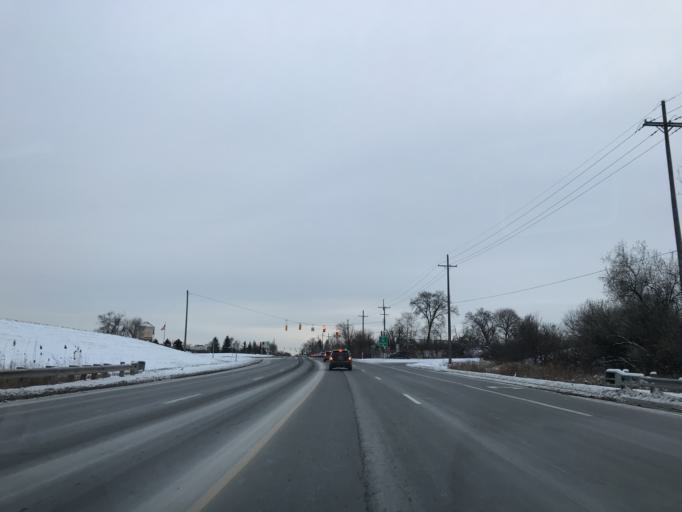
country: US
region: Michigan
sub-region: Oakland County
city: South Lyon
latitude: 42.5186
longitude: -83.6163
